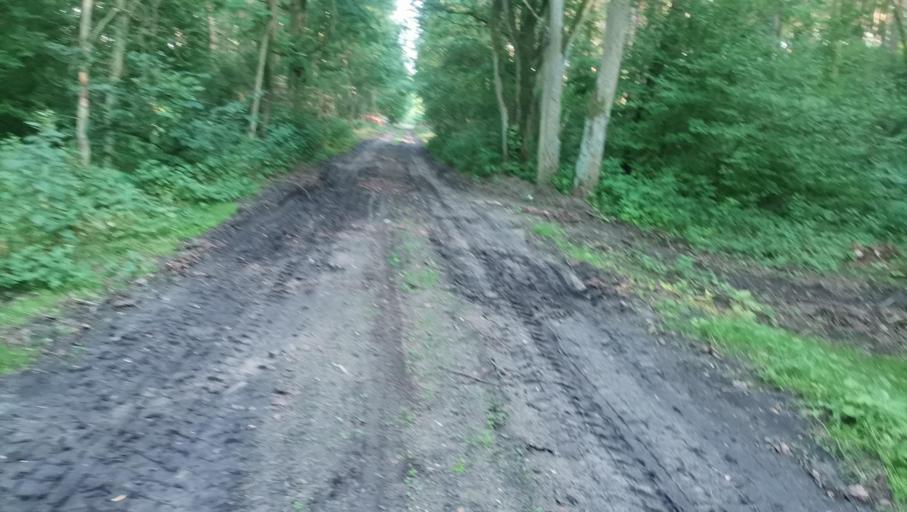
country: PL
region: Greater Poland Voivodeship
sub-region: Powiat jarocinski
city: Jarocin
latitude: 51.9844
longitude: 17.5432
